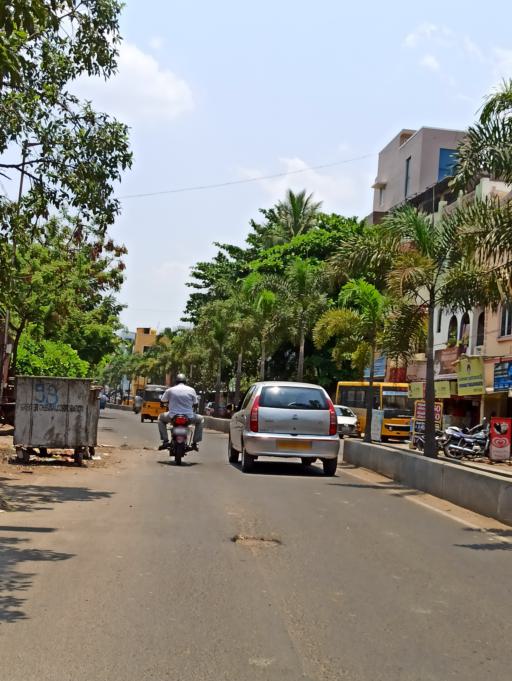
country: IN
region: Tamil Nadu
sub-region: Chennai
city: Chetput
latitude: 13.0930
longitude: 80.2340
